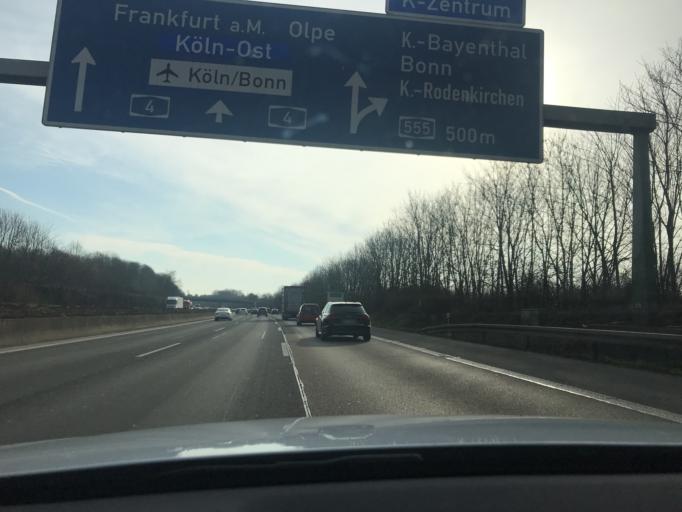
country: DE
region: North Rhine-Westphalia
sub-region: Regierungsbezirk Koln
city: Bayenthal
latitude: 50.8842
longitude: 6.9472
